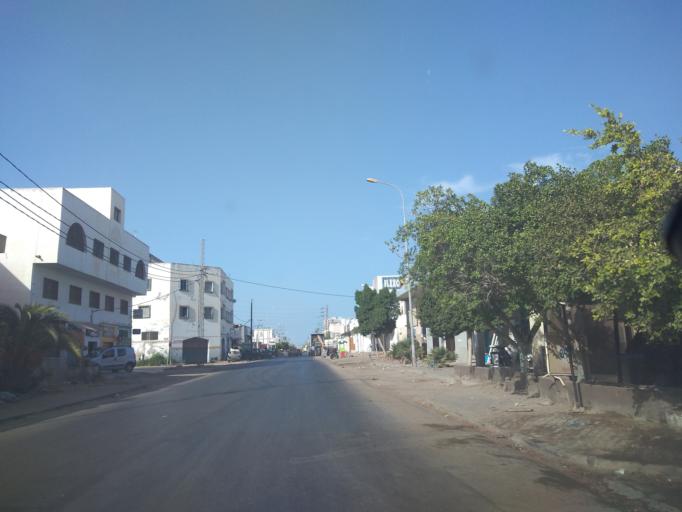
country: TN
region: Safaqis
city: Sfax
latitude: 34.7447
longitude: 10.7682
